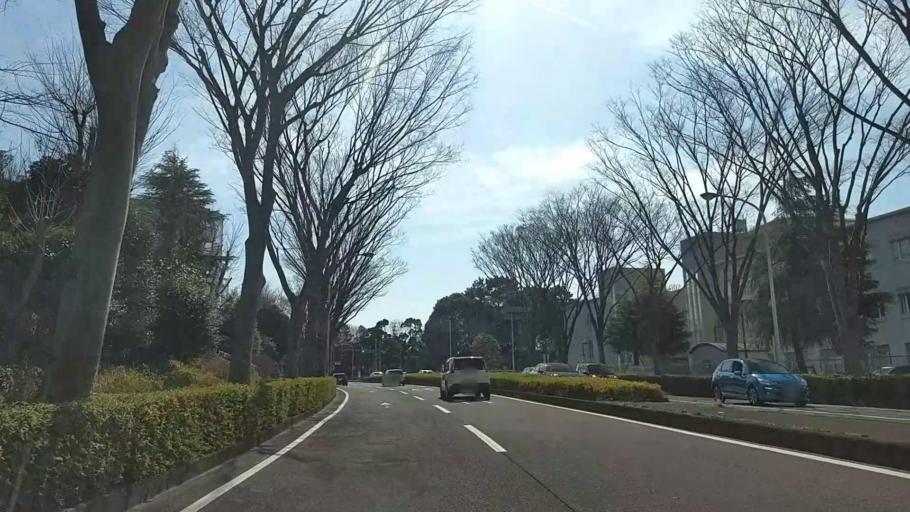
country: JP
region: Kanagawa
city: Fujisawa
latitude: 35.3575
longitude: 139.4431
